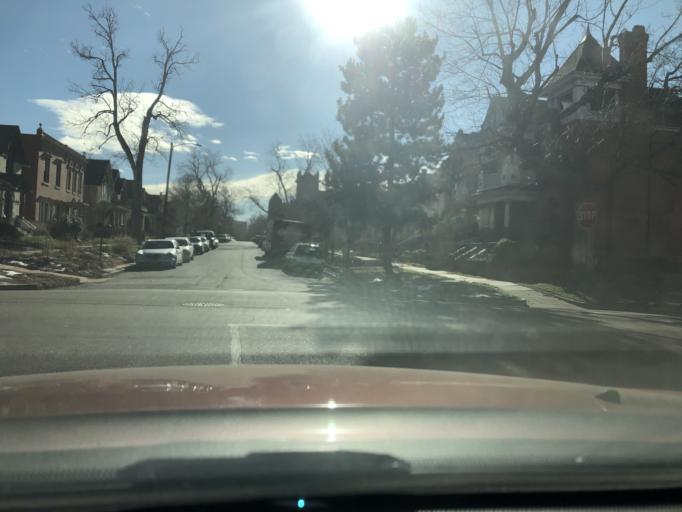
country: US
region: Colorado
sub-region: Denver County
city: Denver
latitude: 39.7522
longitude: -104.9746
